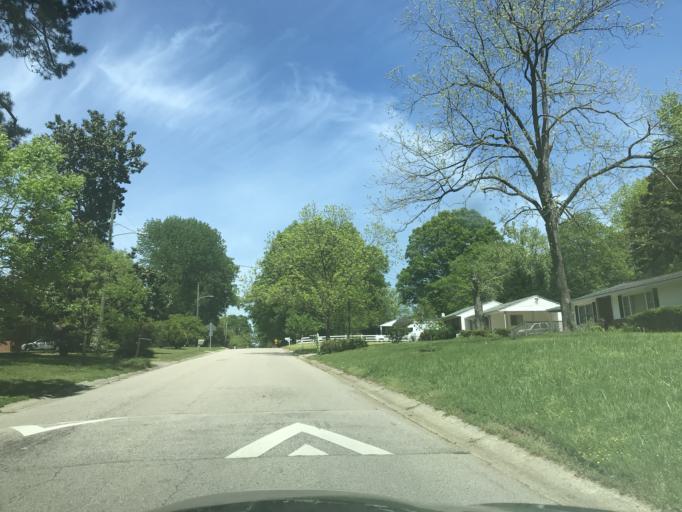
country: US
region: North Carolina
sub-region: Wake County
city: Raleigh
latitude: 35.8277
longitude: -78.5809
